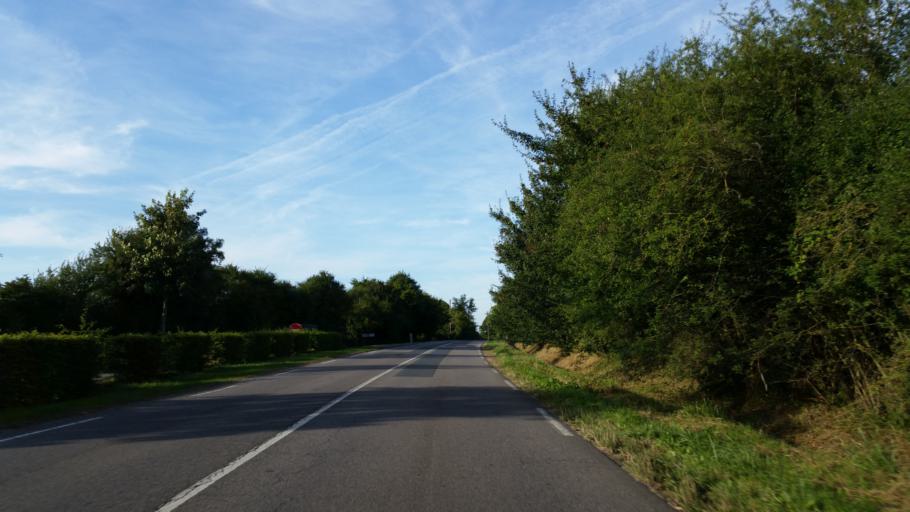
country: FR
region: Lower Normandy
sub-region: Departement du Calvados
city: Cambremer
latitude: 49.1600
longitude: -0.0035
